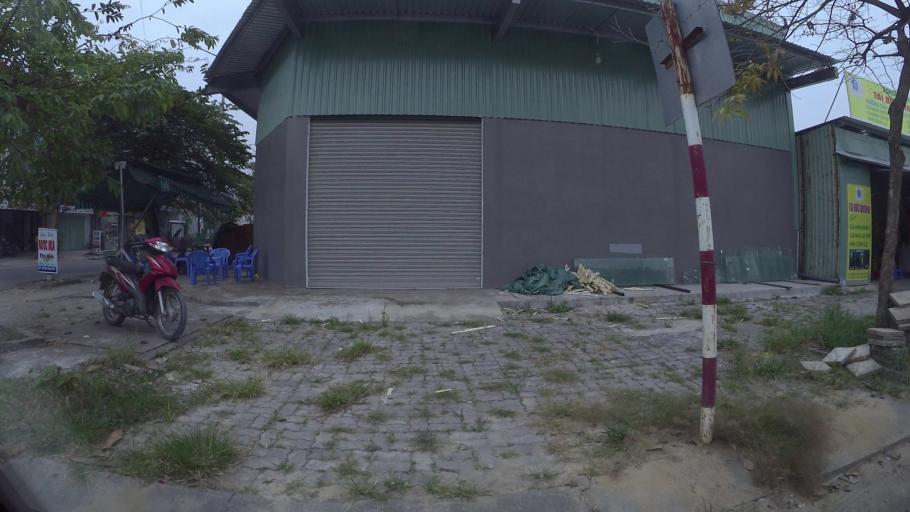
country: VN
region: Da Nang
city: Thanh Khe
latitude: 16.0446
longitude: 108.1787
